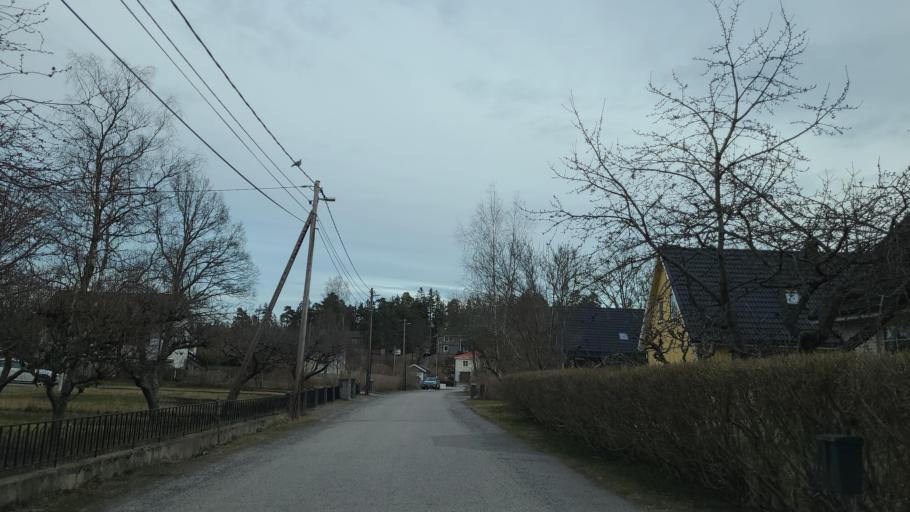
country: SE
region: Stockholm
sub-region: Nacka Kommun
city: Boo
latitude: 59.3191
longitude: 18.2652
